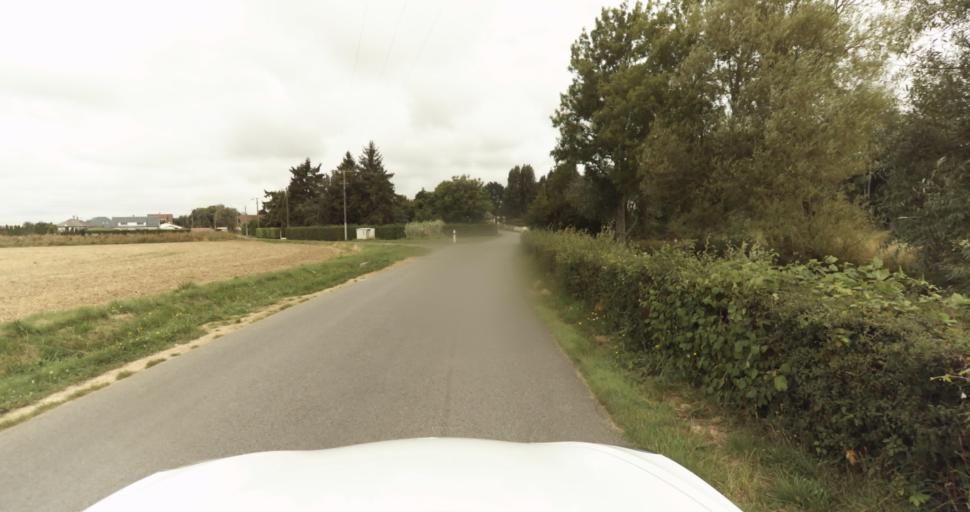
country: FR
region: Haute-Normandie
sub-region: Departement de l'Eure
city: Claville
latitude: 49.0203
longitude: 1.0332
